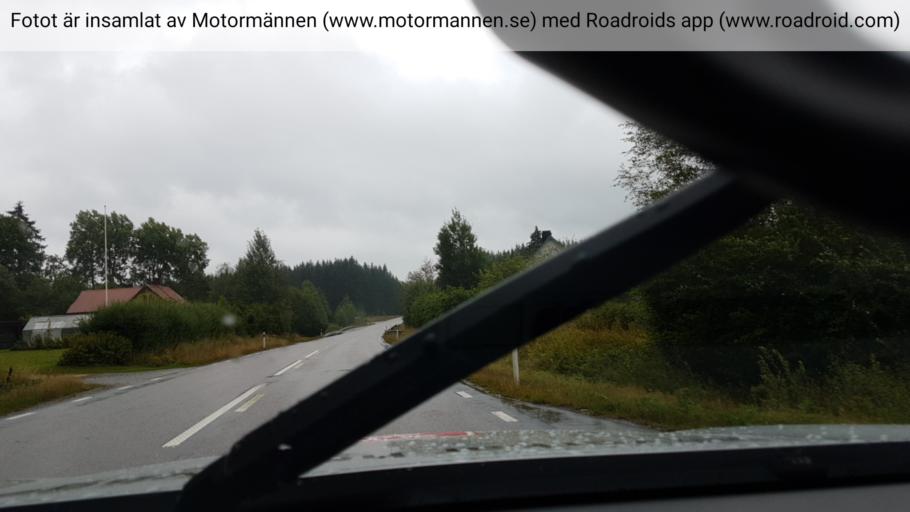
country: SE
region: Vaestra Goetaland
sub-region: Dals-Ed Kommun
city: Ed
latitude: 58.8892
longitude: 11.9180
